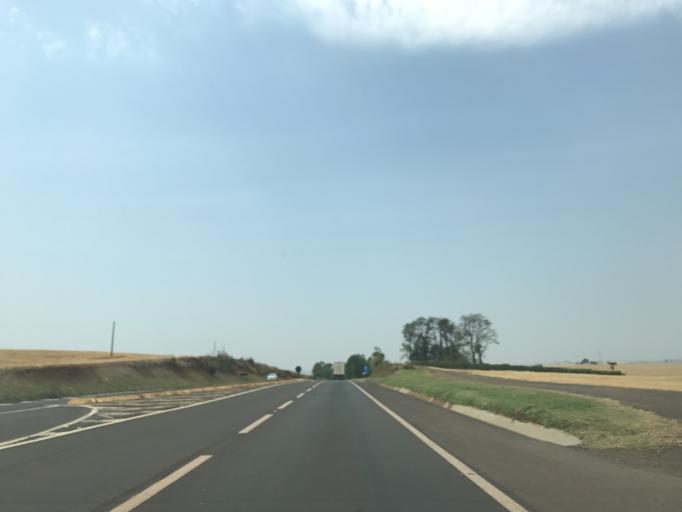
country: BR
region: Parana
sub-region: Rolandia
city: Rolandia
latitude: -23.3395
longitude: -51.3630
